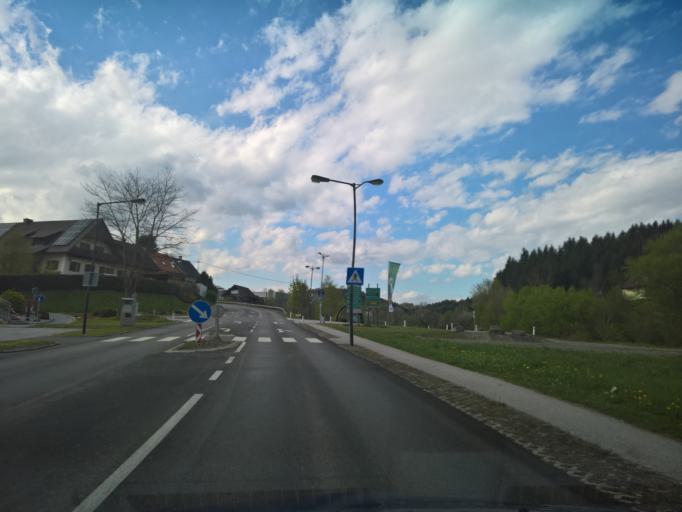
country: AT
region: Styria
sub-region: Politischer Bezirk Deutschlandsberg
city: Sankt Peter im Sulmtal
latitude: 46.7369
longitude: 15.2404
